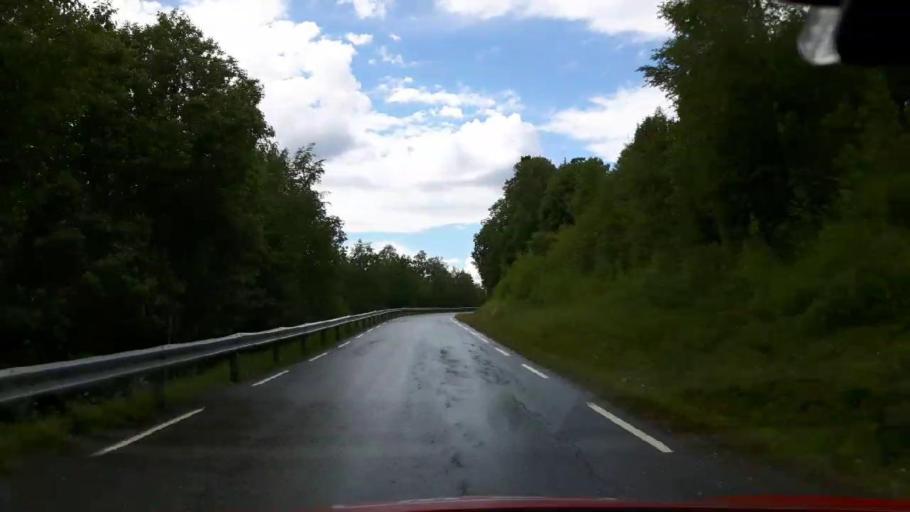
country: NO
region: Nord-Trondelag
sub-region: Lierne
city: Sandvika
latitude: 64.1061
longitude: 13.9886
